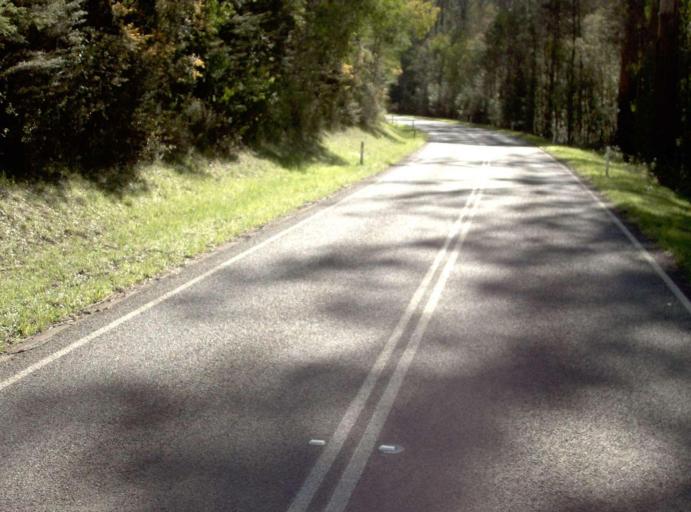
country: AU
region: Victoria
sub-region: Yarra Ranges
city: Millgrove
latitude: -37.8729
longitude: 145.8237
